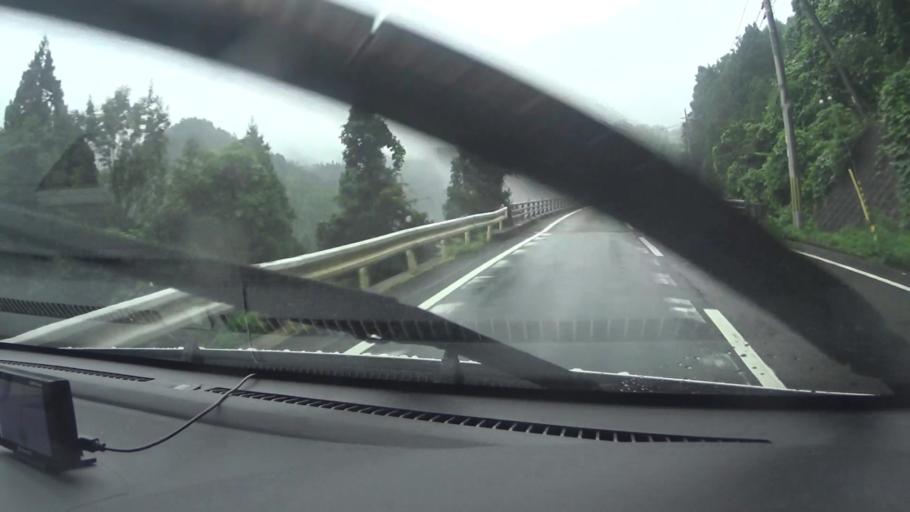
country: JP
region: Kyoto
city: Ayabe
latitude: 35.2792
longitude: 135.2685
